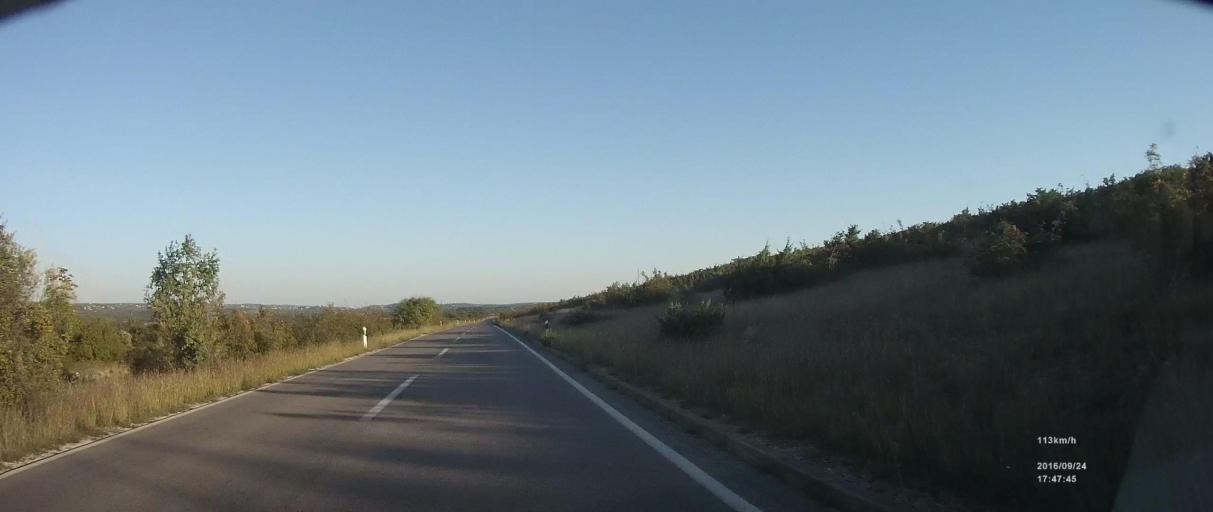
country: HR
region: Zadarska
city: Polaca
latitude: 44.0716
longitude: 15.5276
